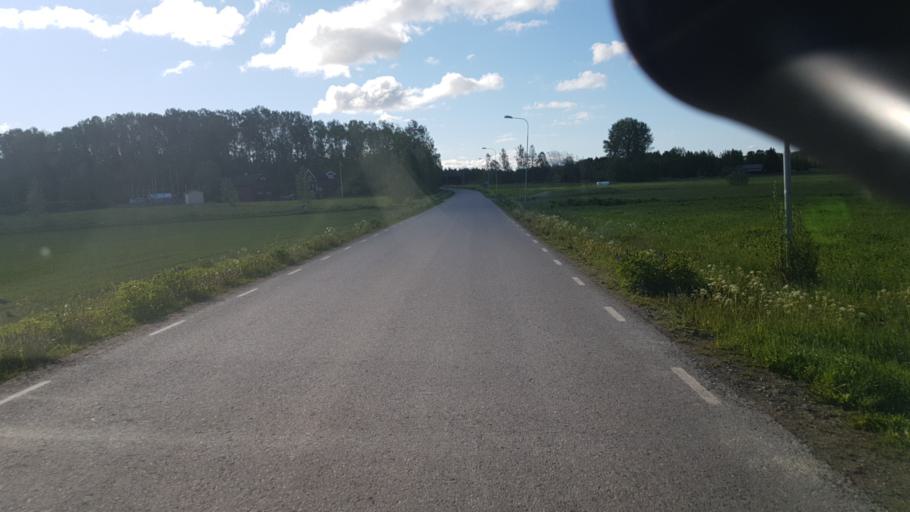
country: SE
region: Vaermland
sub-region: Arvika Kommun
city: Arvika
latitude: 59.5576
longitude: 12.5491
